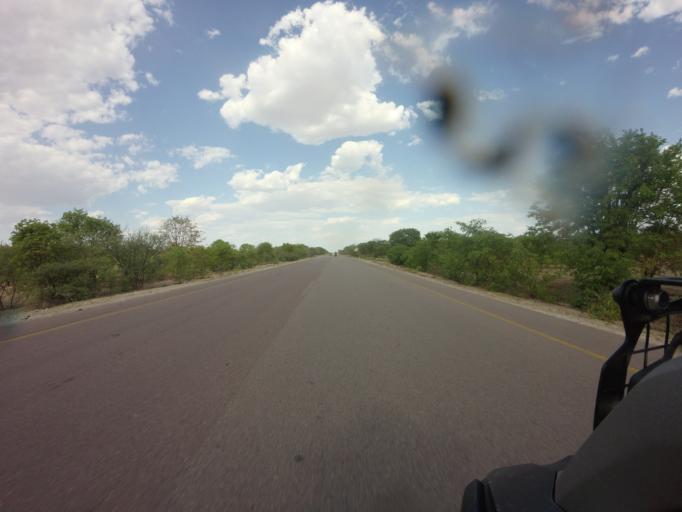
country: AO
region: Cunene
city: Ondjiva
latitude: -16.7302
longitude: 15.1733
